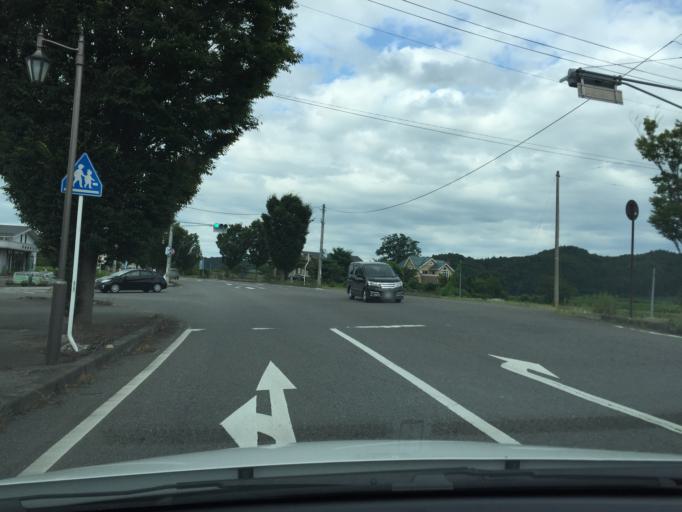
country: JP
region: Fukushima
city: Sukagawa
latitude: 37.2009
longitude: 140.2460
